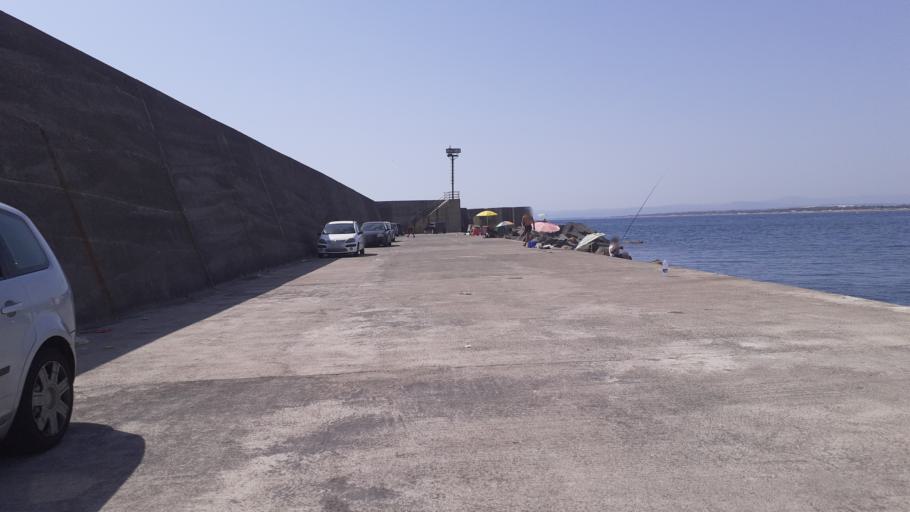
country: IT
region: Sicily
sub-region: Catania
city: Catania
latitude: 37.4850
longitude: 15.0994
